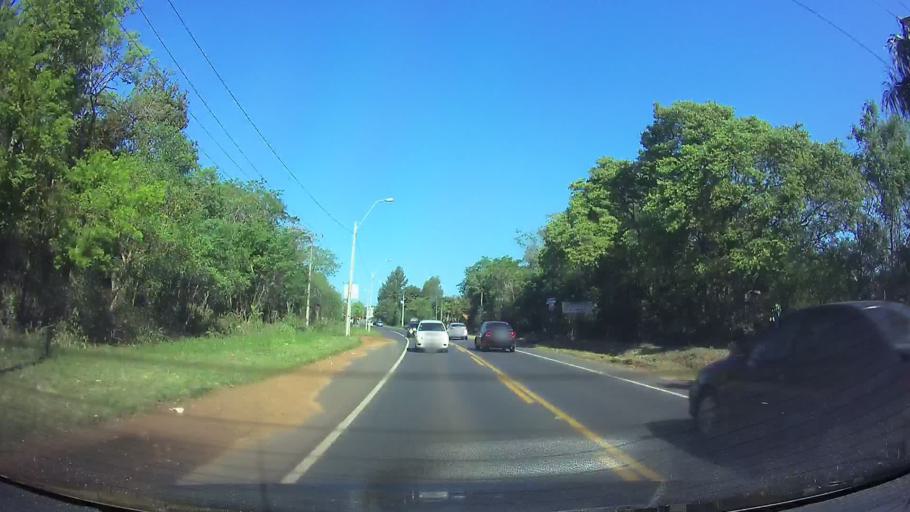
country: PY
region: Central
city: Aregua
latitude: -25.3396
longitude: -57.3492
